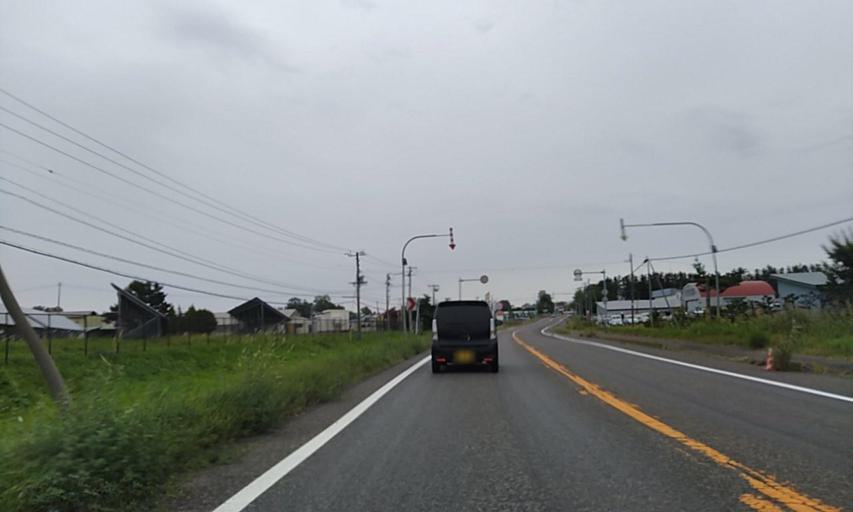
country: JP
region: Hokkaido
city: Bihoro
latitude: 43.9159
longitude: 144.1618
